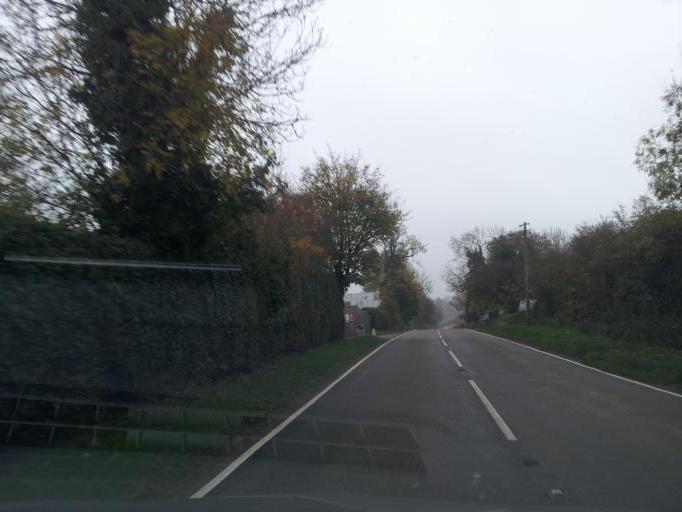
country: GB
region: England
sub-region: Northamptonshire
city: Brackley
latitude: 52.0196
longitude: -1.0830
